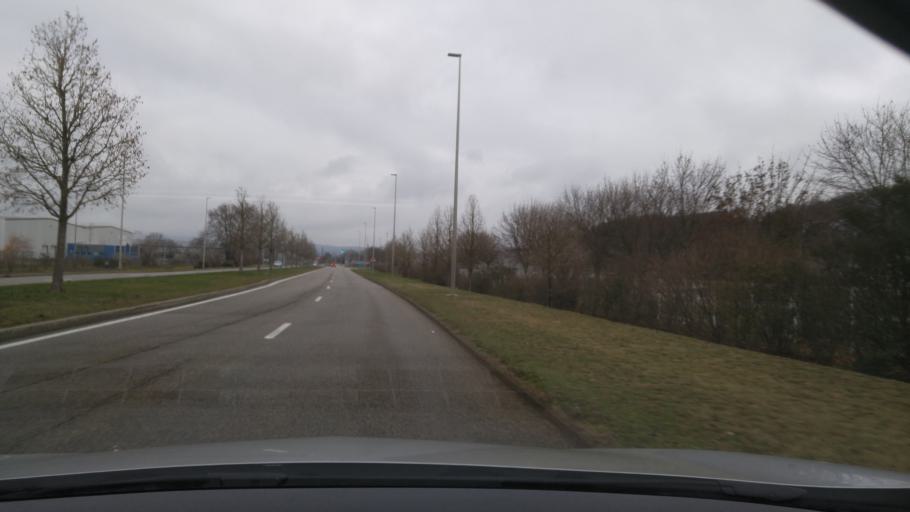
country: FR
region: Rhone-Alpes
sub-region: Departement de l'Isere
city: Saint-Quentin-Fallavier
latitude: 45.6395
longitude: 5.1113
